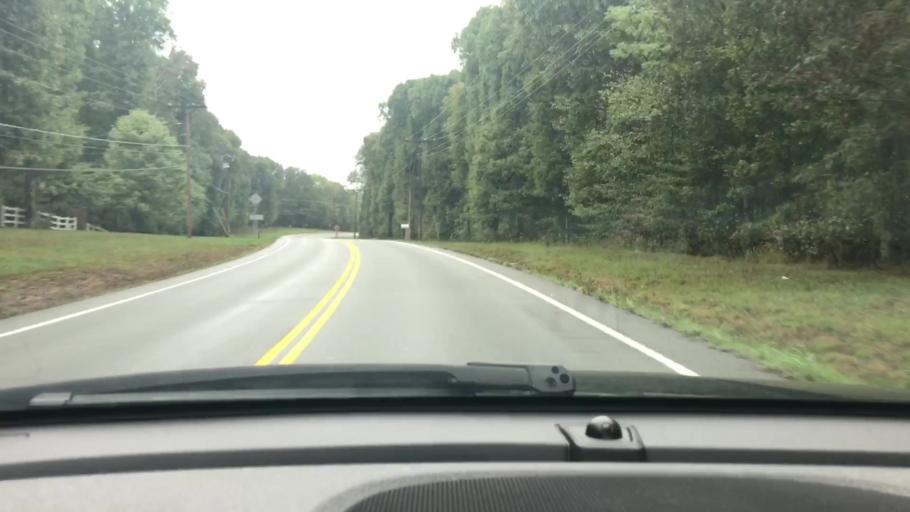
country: US
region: Tennessee
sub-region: Cheatham County
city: Kingston Springs
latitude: 36.1099
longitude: -87.1648
